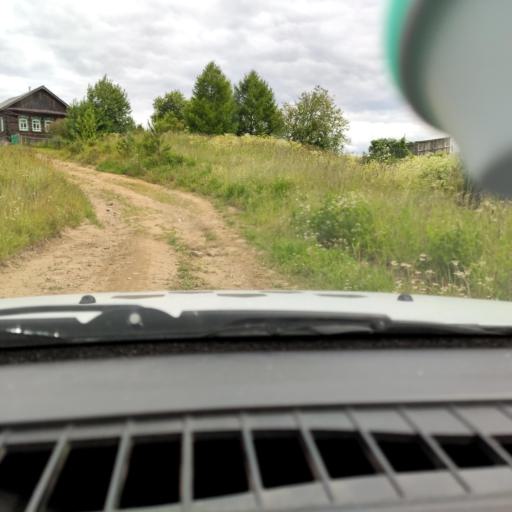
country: RU
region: Perm
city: Suksun
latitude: 57.2100
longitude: 57.7025
